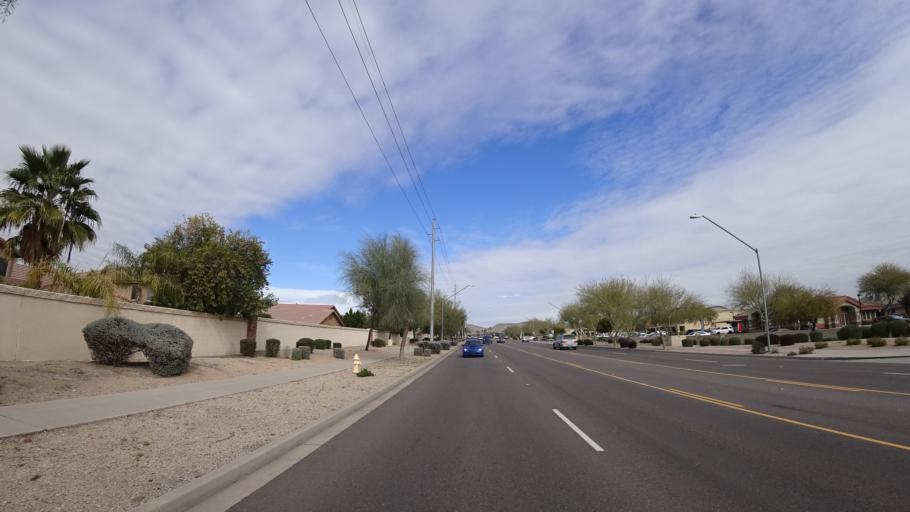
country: US
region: Arizona
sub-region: Maricopa County
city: Peoria
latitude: 33.6514
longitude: -112.1864
